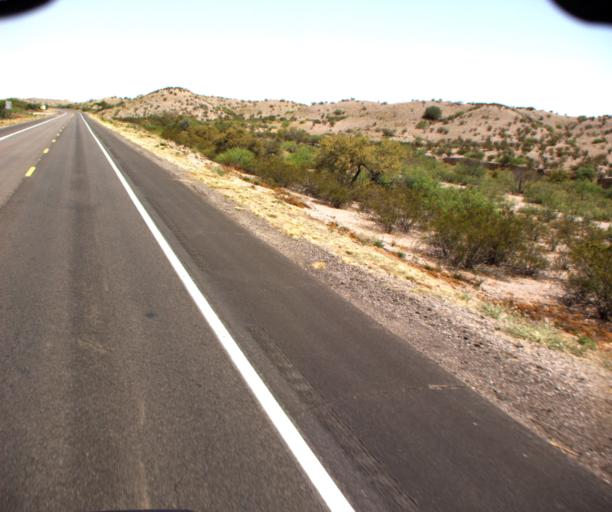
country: US
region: New Mexico
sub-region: Hidalgo County
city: Lordsburg
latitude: 32.6491
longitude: -109.0513
